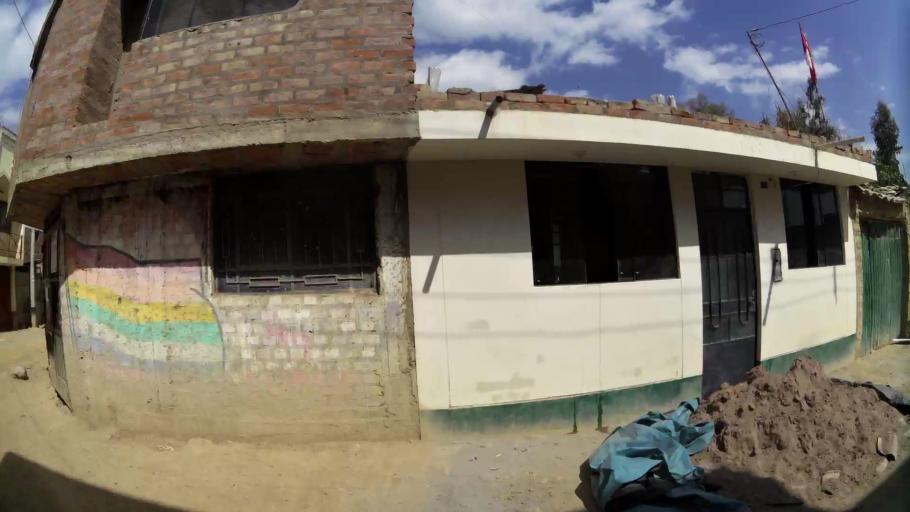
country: PE
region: Junin
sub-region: Provincia de Huancayo
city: Huancayo
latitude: -12.0919
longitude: -75.2004
